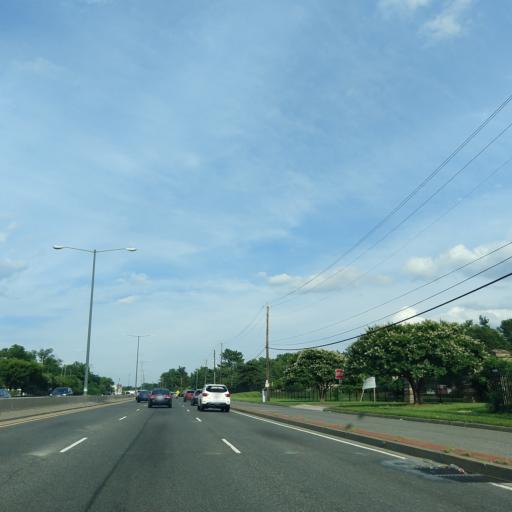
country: US
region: Maryland
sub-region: Prince George's County
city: Colmar Manor
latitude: 38.9167
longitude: -76.9627
